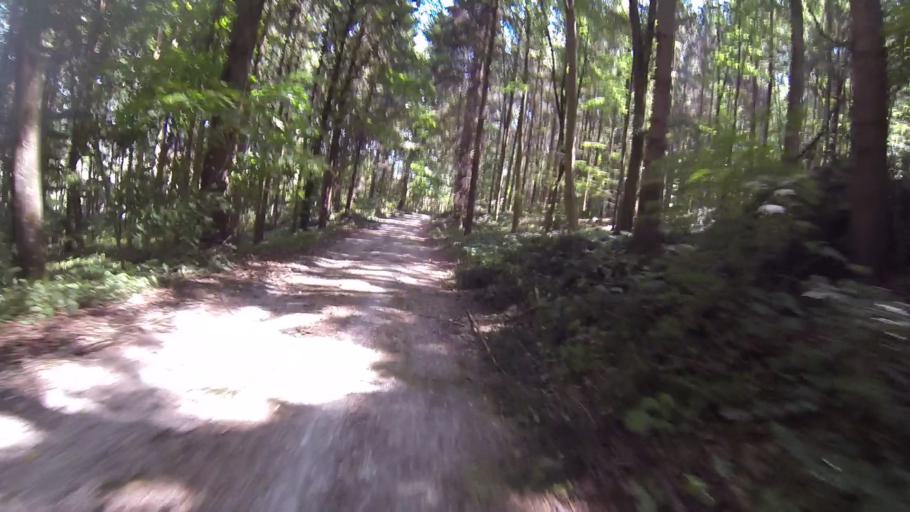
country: DE
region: Baden-Wuerttemberg
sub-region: Regierungsbezirk Stuttgart
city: Giengen an der Brenz
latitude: 48.6370
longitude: 10.2187
